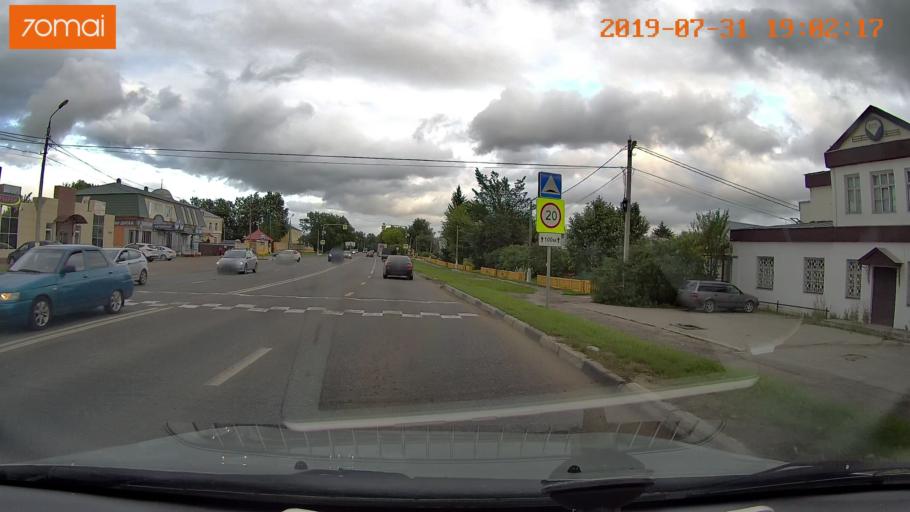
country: RU
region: Moskovskaya
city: Raduzhnyy
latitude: 55.1206
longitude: 38.7316
